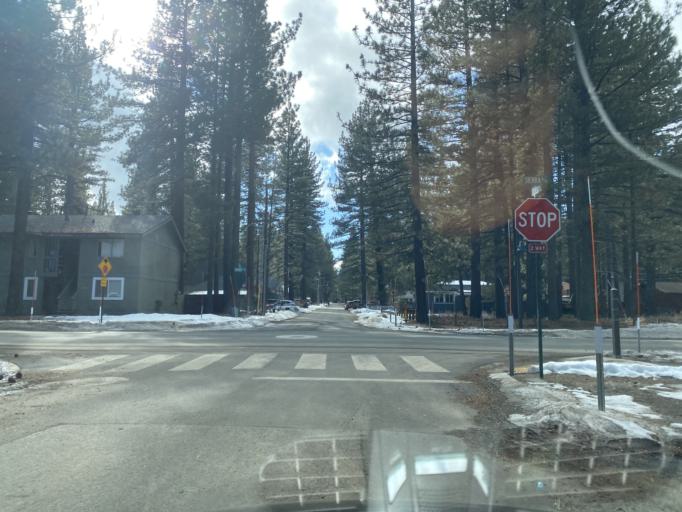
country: US
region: California
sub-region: El Dorado County
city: South Lake Tahoe
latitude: 38.9191
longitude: -119.9791
